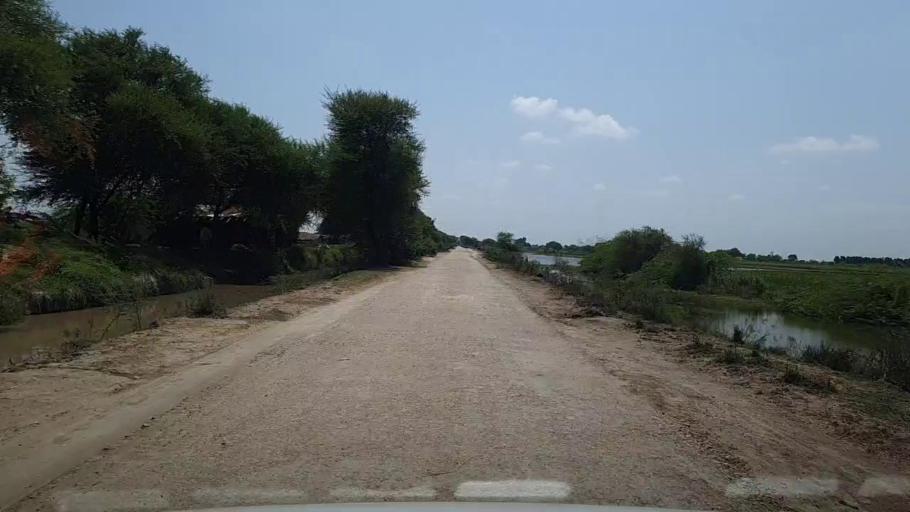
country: PK
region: Sindh
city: Kario
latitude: 24.8749
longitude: 68.6881
